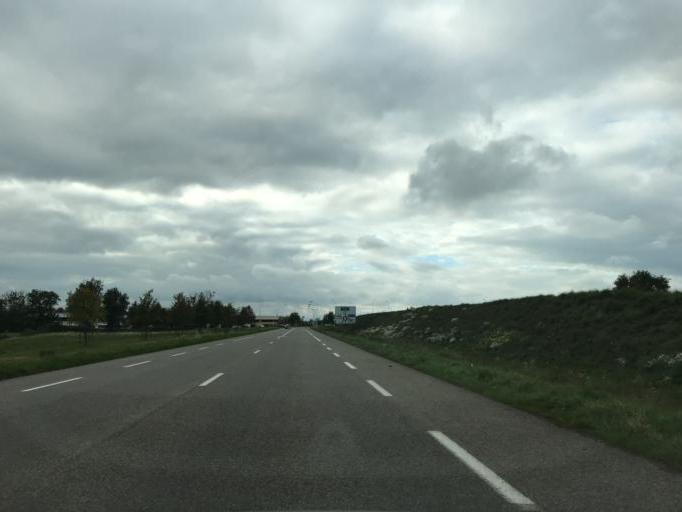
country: FR
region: Rhone-Alpes
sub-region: Departement de l'Ain
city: Bourg-en-Bresse
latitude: 46.2205
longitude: 5.2535
